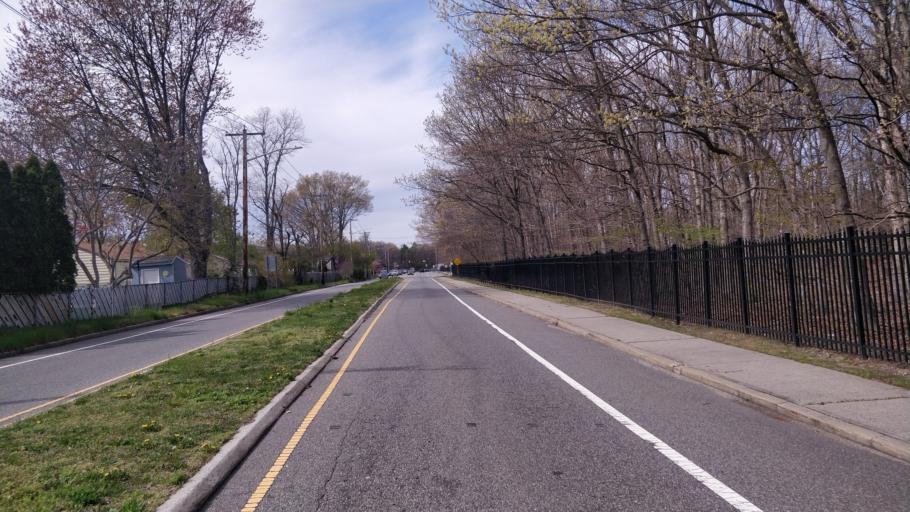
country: US
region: New York
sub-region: Suffolk County
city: Terryville
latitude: 40.8962
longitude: -73.0799
